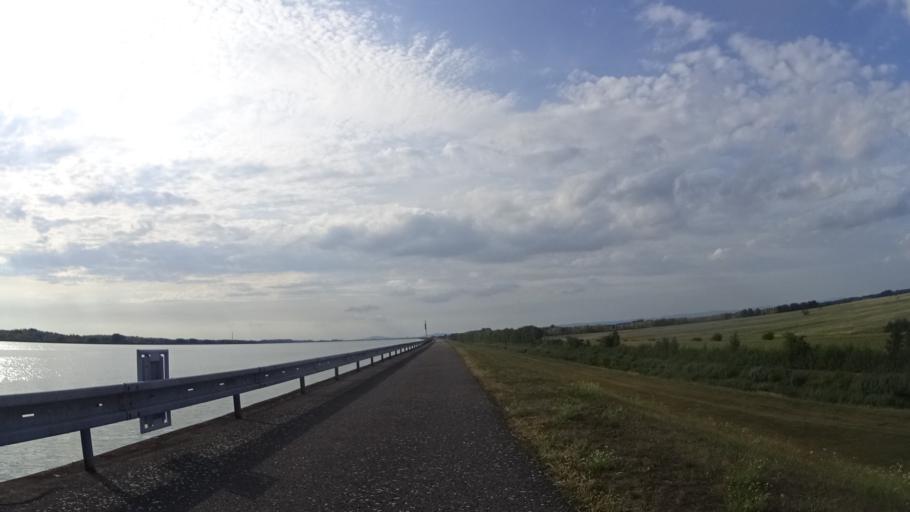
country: HU
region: Gyor-Moson-Sopron
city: Halaszi
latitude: 47.9551
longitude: 17.4321
